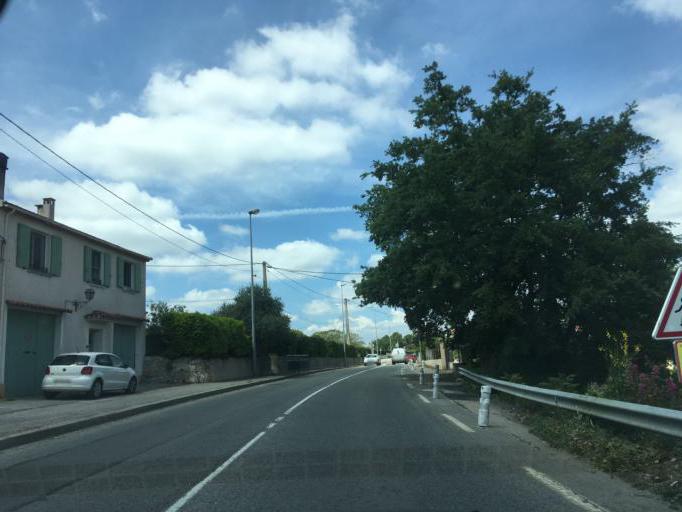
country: FR
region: Provence-Alpes-Cote d'Azur
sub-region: Departement du Var
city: Flayosc
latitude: 43.5359
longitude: 6.3909
